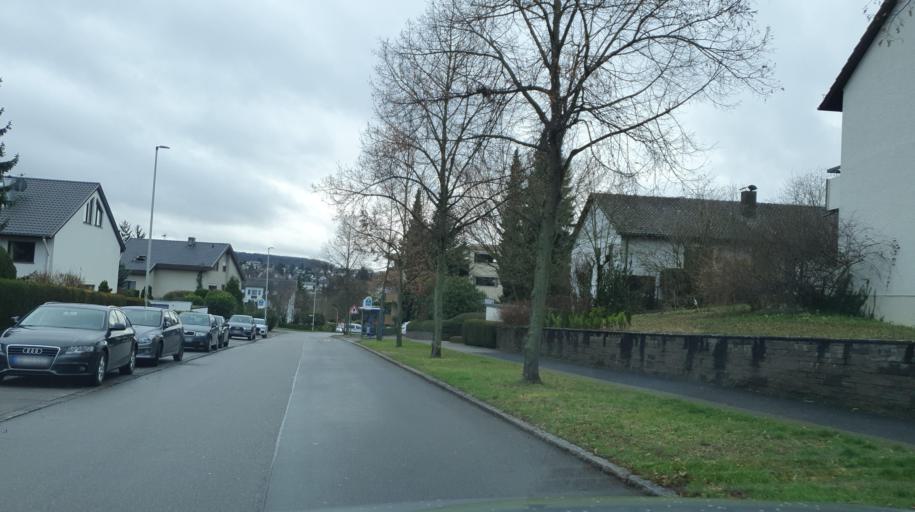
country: DE
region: Baden-Wuerttemberg
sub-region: Regierungsbezirk Stuttgart
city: Heilbronn
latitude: 49.1441
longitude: 9.2486
